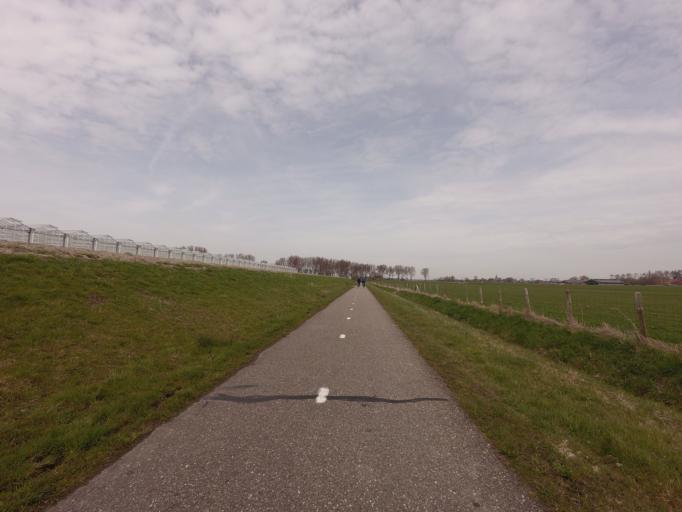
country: NL
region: South Holland
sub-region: Gemeente Westland
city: De Lier
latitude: 51.9861
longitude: 4.2910
